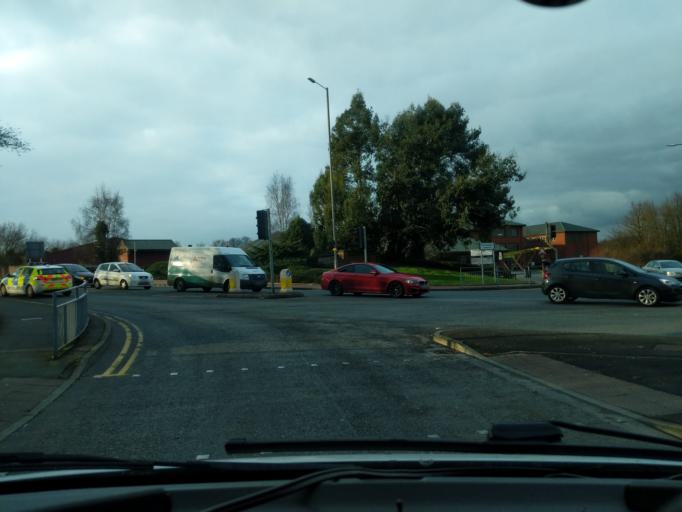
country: GB
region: England
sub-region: St. Helens
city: St Helens
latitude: 53.4559
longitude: -2.7251
